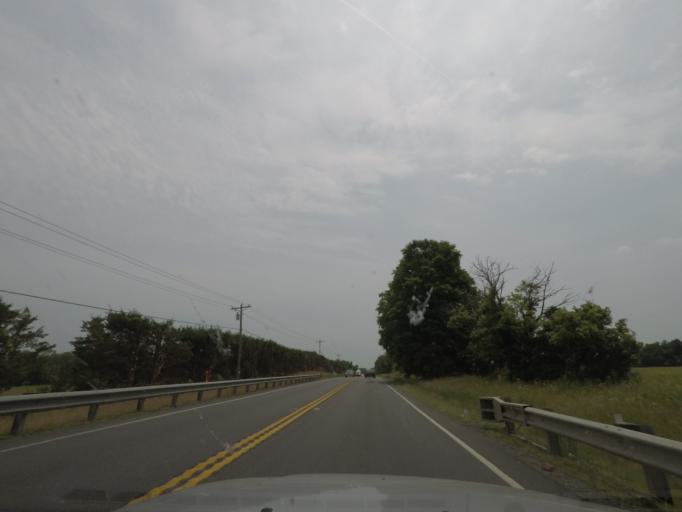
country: US
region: Virginia
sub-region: Prince William County
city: Bull Run Mountain Estates
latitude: 38.8984
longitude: -77.6307
